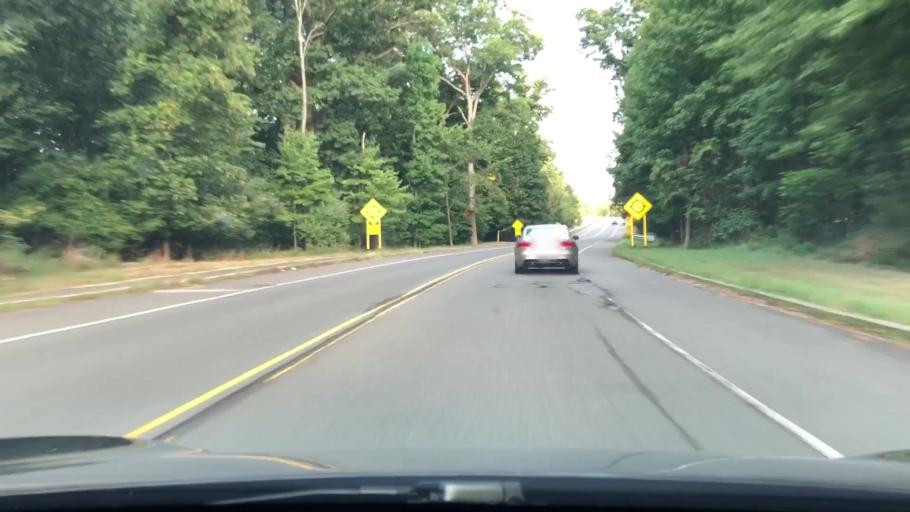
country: US
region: New Jersey
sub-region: Mercer County
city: Pennington
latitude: 40.3021
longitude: -74.7732
